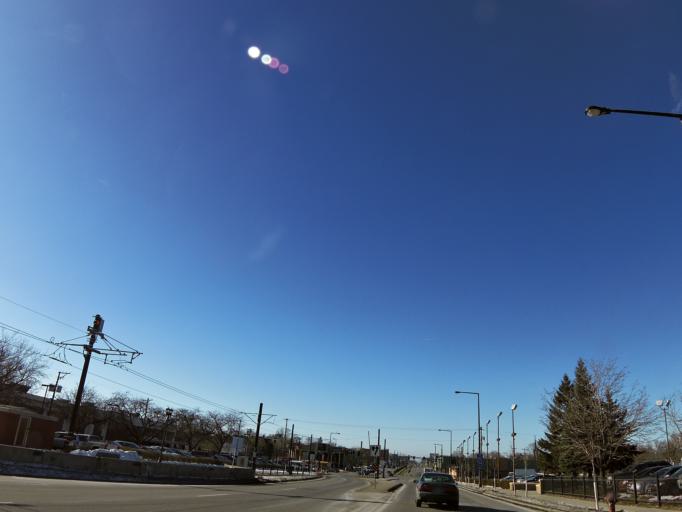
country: US
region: Minnesota
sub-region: Ramsey County
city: Saint Paul
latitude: 44.9559
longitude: -93.1072
